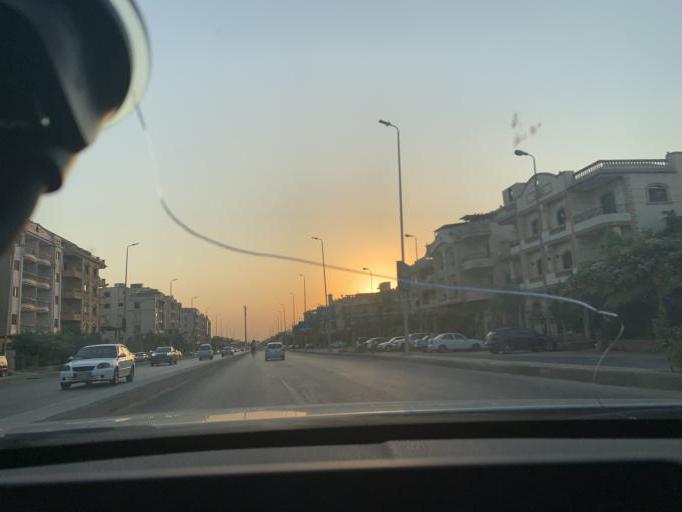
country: EG
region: Muhafazat al Qahirah
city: Cairo
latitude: 30.0060
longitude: 31.4510
